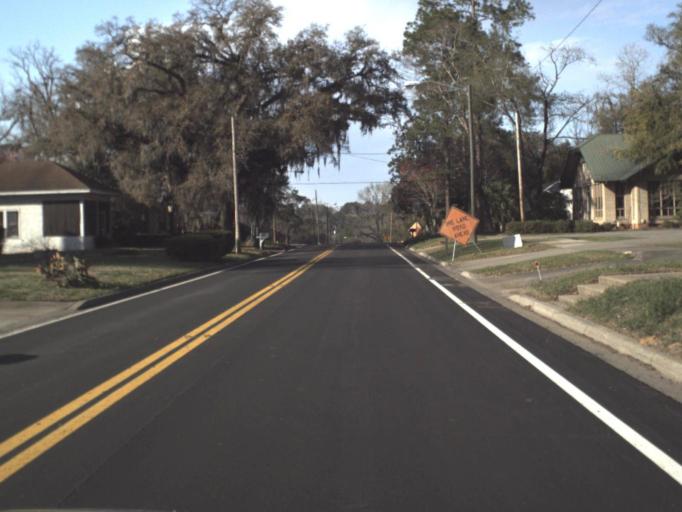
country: US
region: Florida
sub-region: Jackson County
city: Marianna
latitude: 30.7790
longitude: -85.2267
